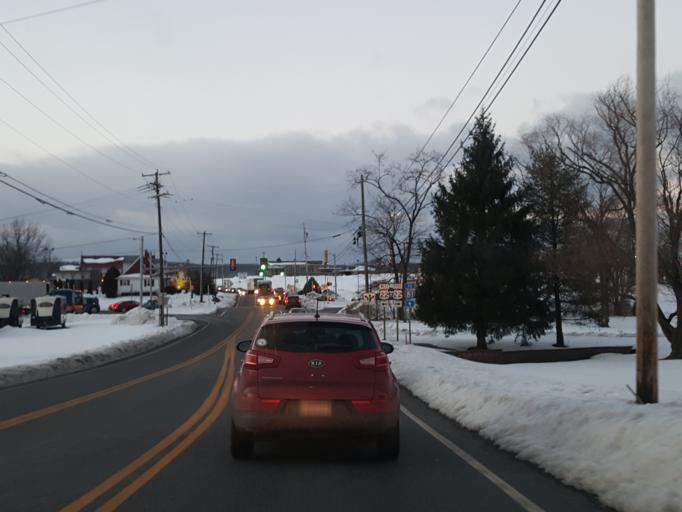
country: US
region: Pennsylvania
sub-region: Dauphin County
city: Palmdale
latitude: 40.3705
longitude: -76.6503
